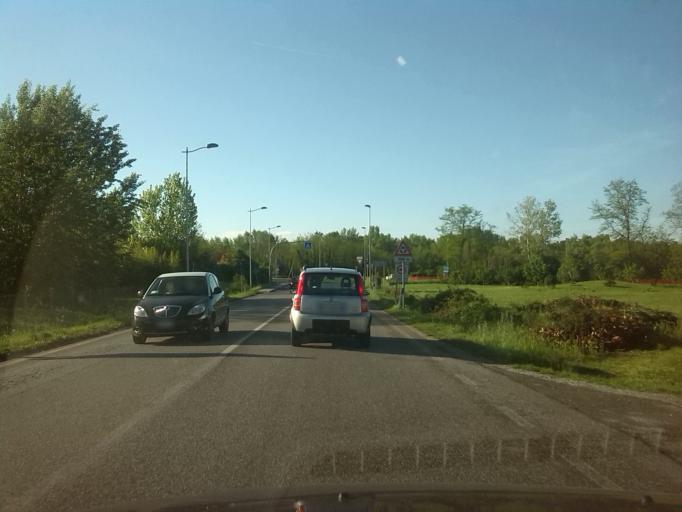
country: IT
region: Friuli Venezia Giulia
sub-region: Provincia di Gorizia
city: Sagrado
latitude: 45.8819
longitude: 13.4817
